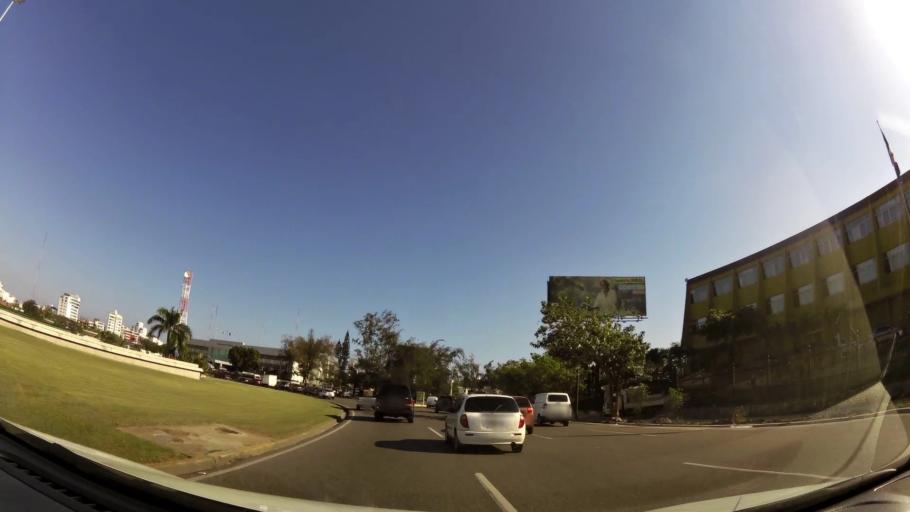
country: DO
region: Nacional
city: Bella Vista
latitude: 18.4492
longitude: -69.9759
